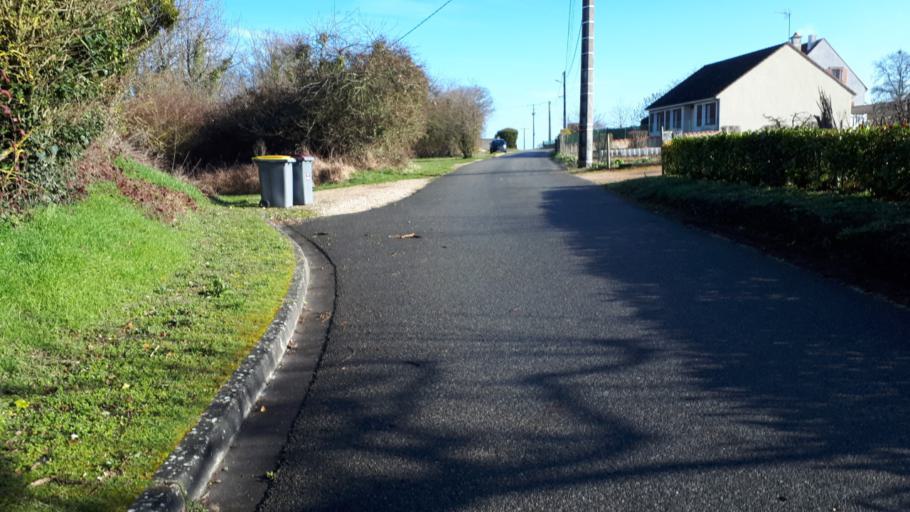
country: FR
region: Centre
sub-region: Departement du Loir-et-Cher
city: Villiers-sur-Loir
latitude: 47.7917
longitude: 0.9663
